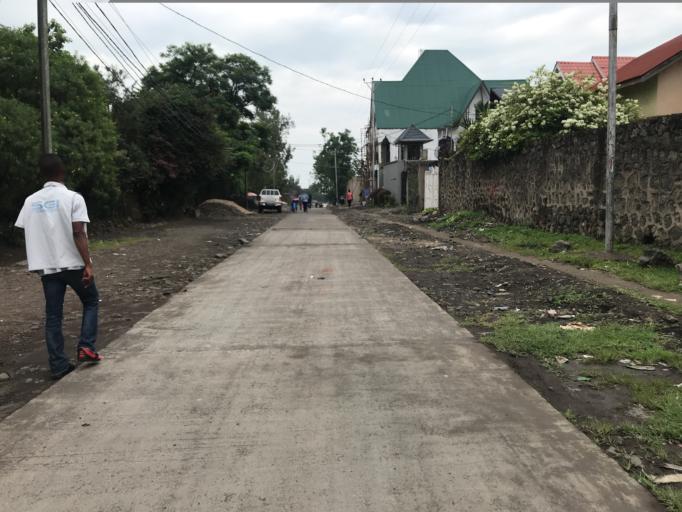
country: CD
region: Nord Kivu
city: Goma
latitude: -1.6866
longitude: 29.2326
